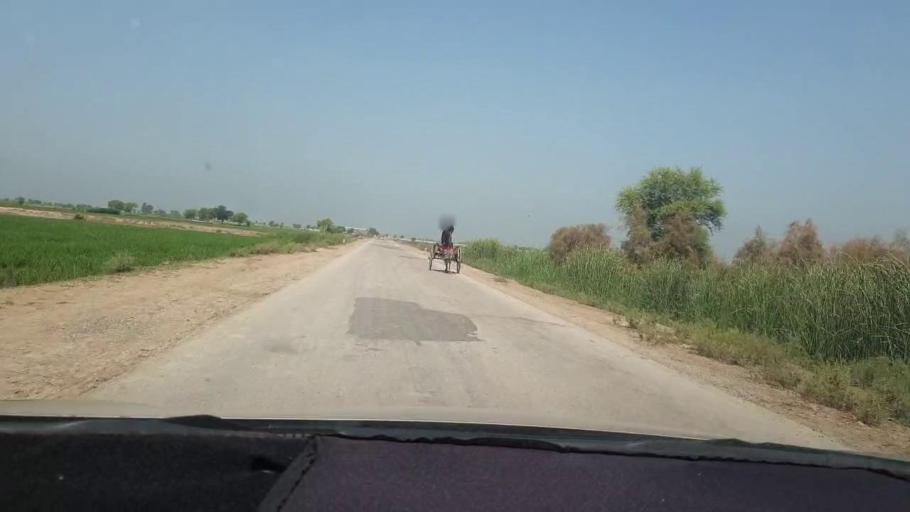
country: PK
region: Sindh
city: Shahdadkot
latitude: 27.8417
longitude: 68.0059
